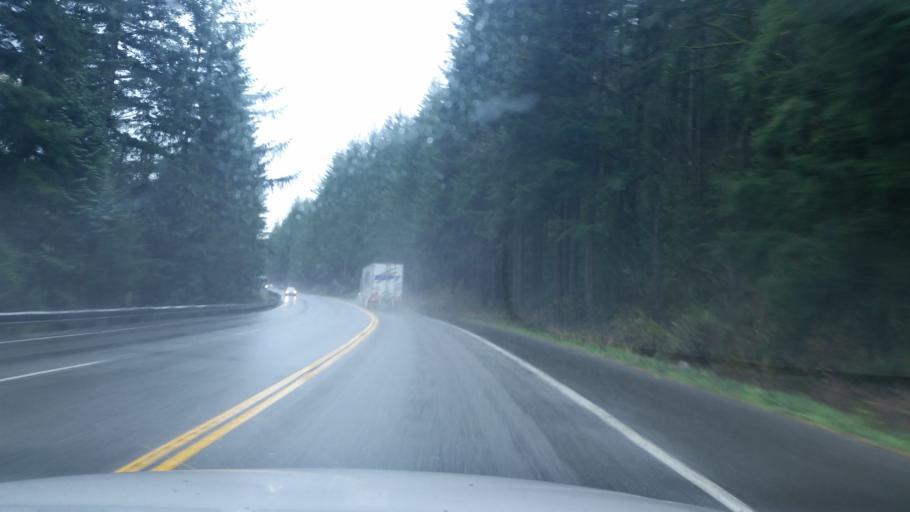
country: US
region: Washington
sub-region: King County
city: Hobart
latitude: 47.4478
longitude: -121.9601
